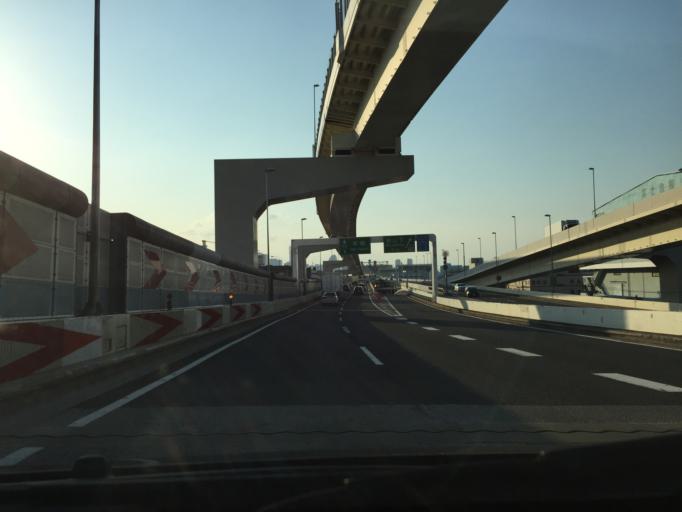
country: JP
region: Kanagawa
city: Yokohama
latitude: 35.4378
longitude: 139.6637
